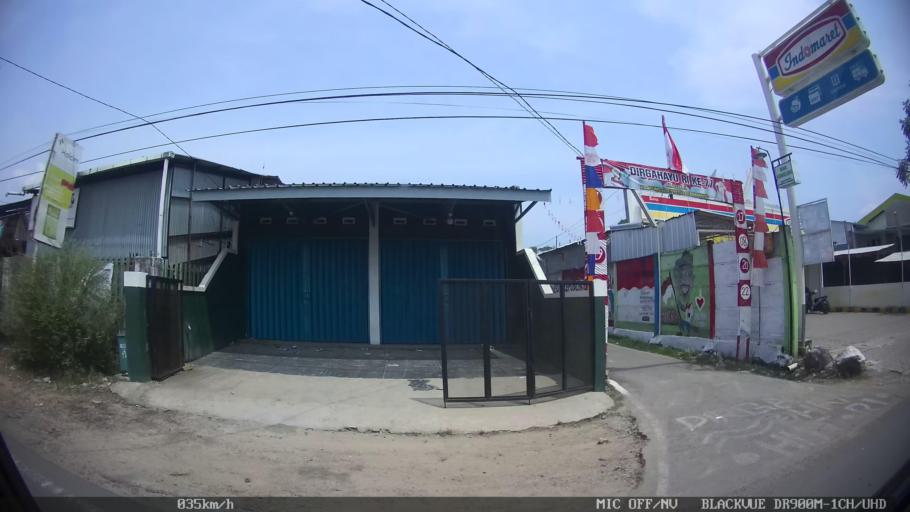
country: ID
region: Lampung
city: Bandarlampung
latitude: -5.4525
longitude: 105.2492
